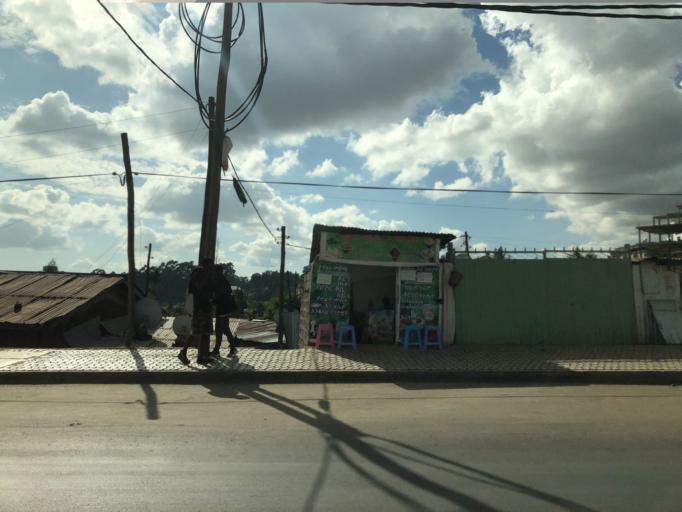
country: ET
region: Adis Abeba
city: Addis Ababa
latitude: 9.0306
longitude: 38.7738
